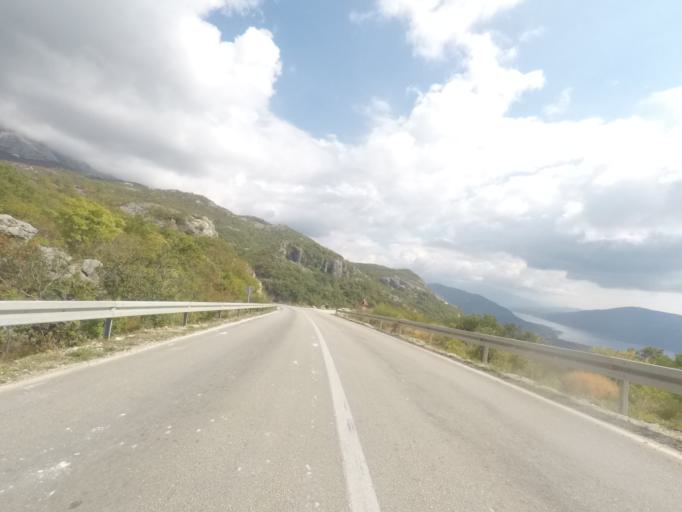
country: ME
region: Herceg Novi
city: Herceg-Novi
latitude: 42.4735
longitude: 18.5303
